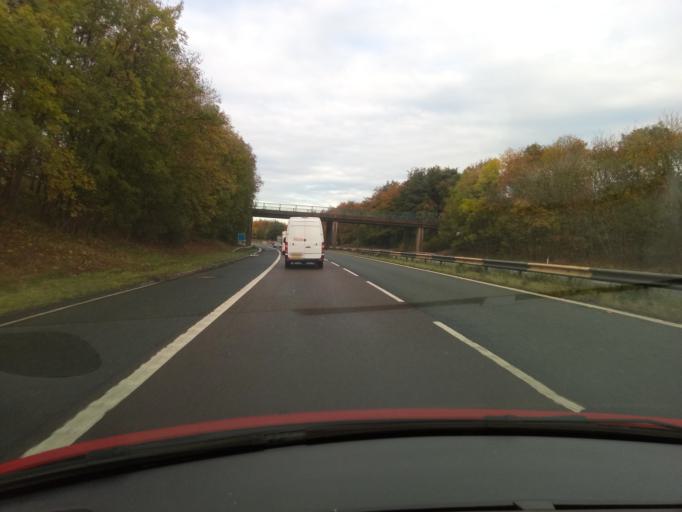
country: GB
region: England
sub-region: Darlington
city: High Coniscliffe
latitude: 54.5088
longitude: -1.6202
